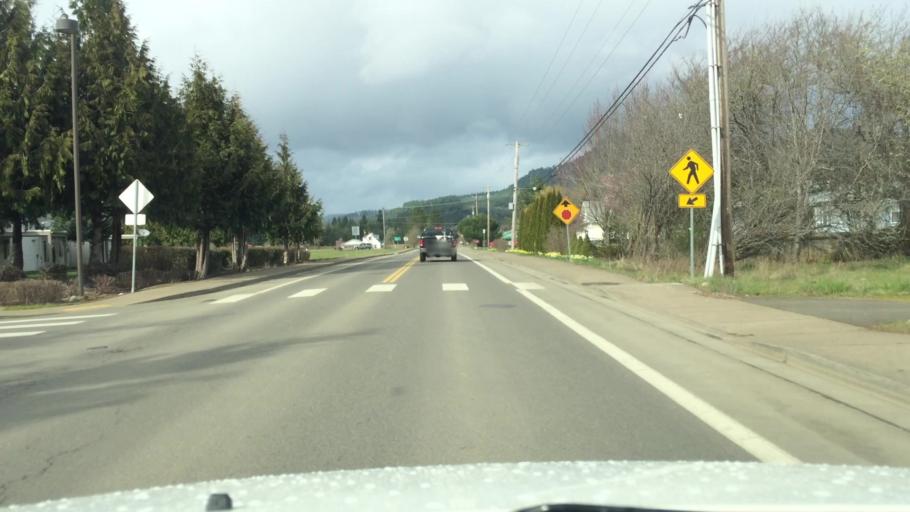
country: US
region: Oregon
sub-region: Polk County
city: Grand Ronde
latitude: 45.0779
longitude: -123.6119
